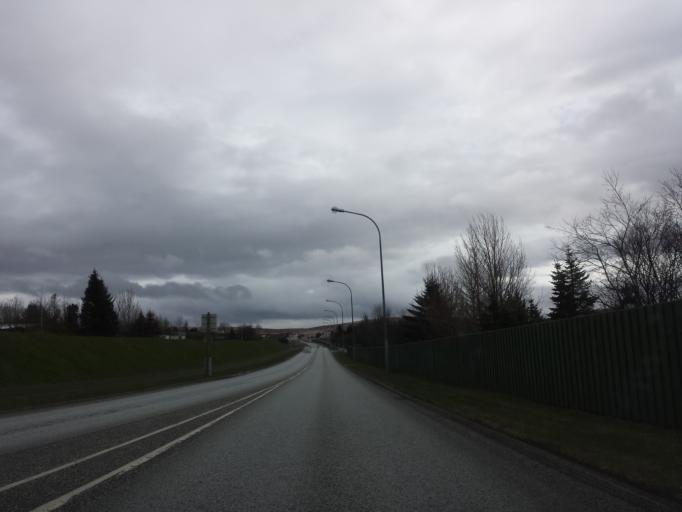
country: IS
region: Capital Region
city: Gardabaer
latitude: 64.0848
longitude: -21.9078
